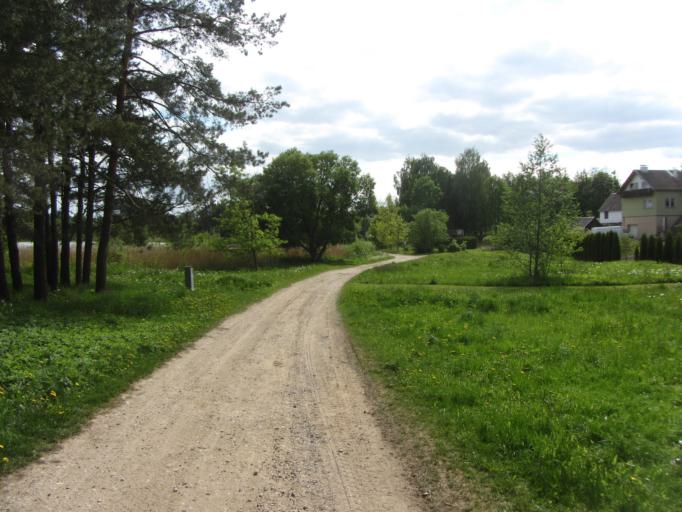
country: LT
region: Utenos apskritis
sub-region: Utena
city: Utena
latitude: 55.4939
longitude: 25.5912
